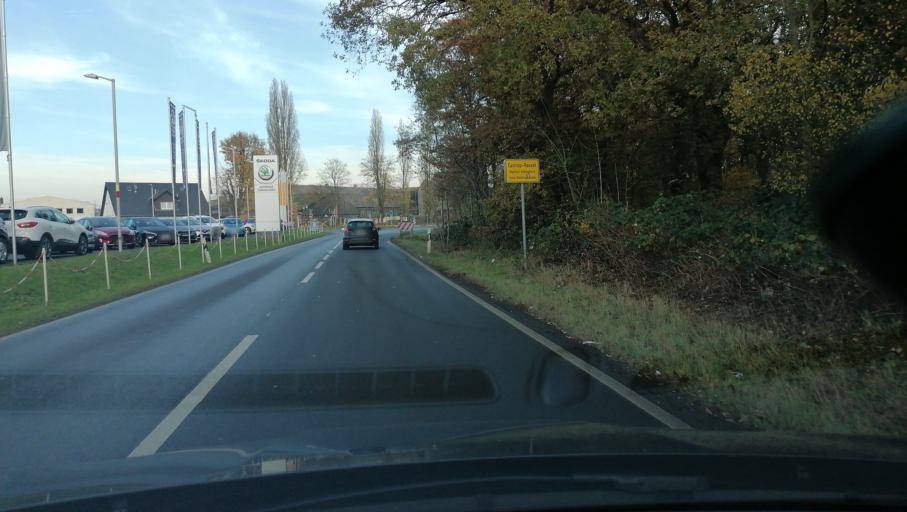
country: DE
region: North Rhine-Westphalia
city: Castrop-Rauxel
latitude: 51.5878
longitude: 7.3005
